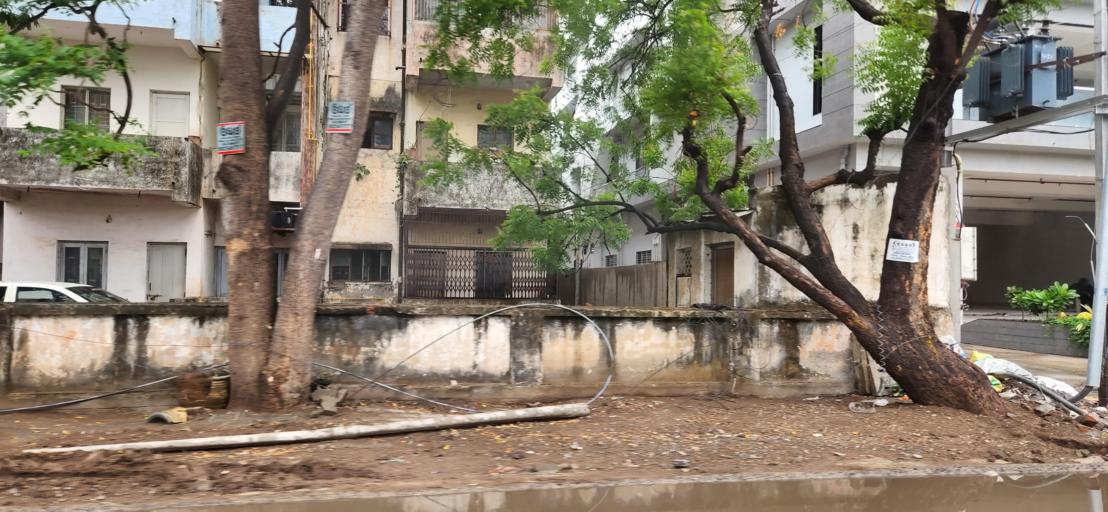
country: IN
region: Gujarat
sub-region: Bhavnagar
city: Bhavnagar
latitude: 21.7569
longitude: 72.1445
